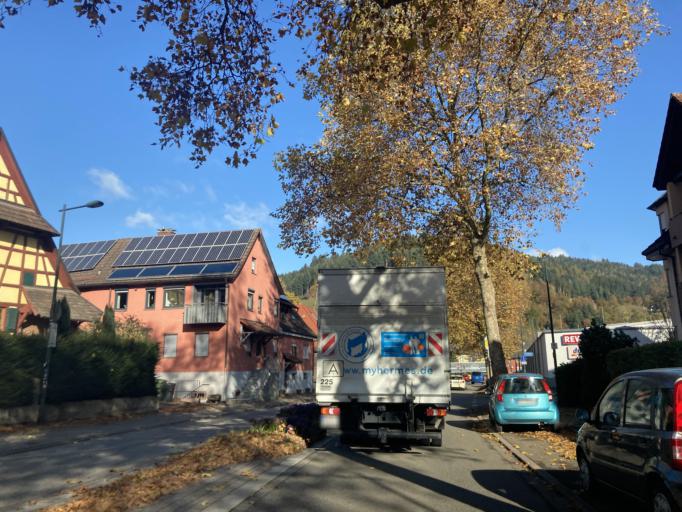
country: DE
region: Baden-Wuerttemberg
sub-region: Freiburg Region
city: Hofstetten
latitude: 48.2780
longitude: 8.0900
